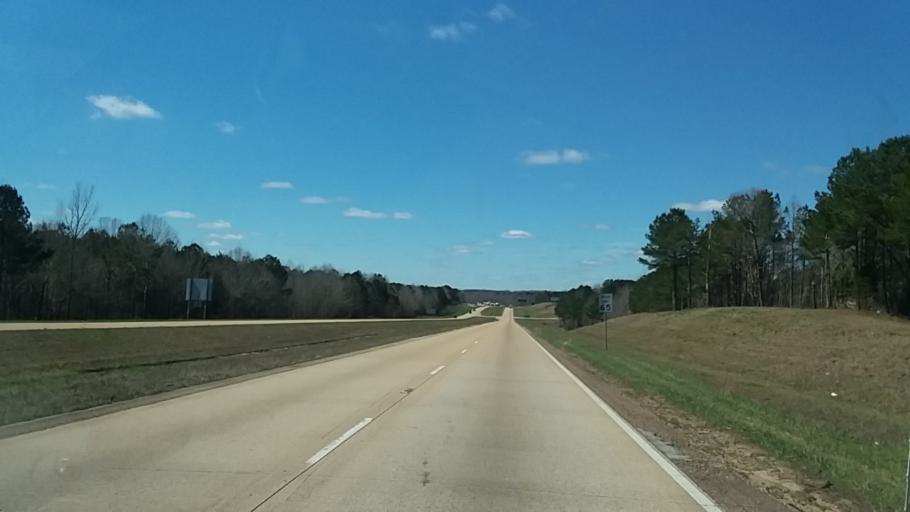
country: US
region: Mississippi
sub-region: Tishomingo County
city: Iuka
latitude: 34.7977
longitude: -88.2200
